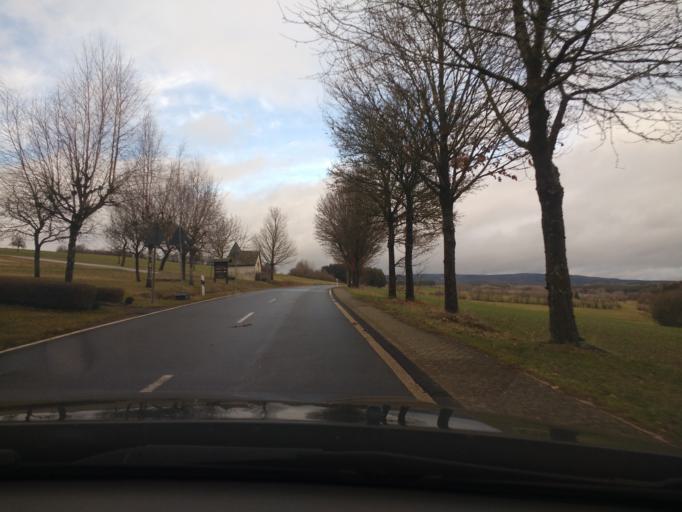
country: DE
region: Rheinland-Pfalz
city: Schillingen
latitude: 49.6229
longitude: 6.7868
